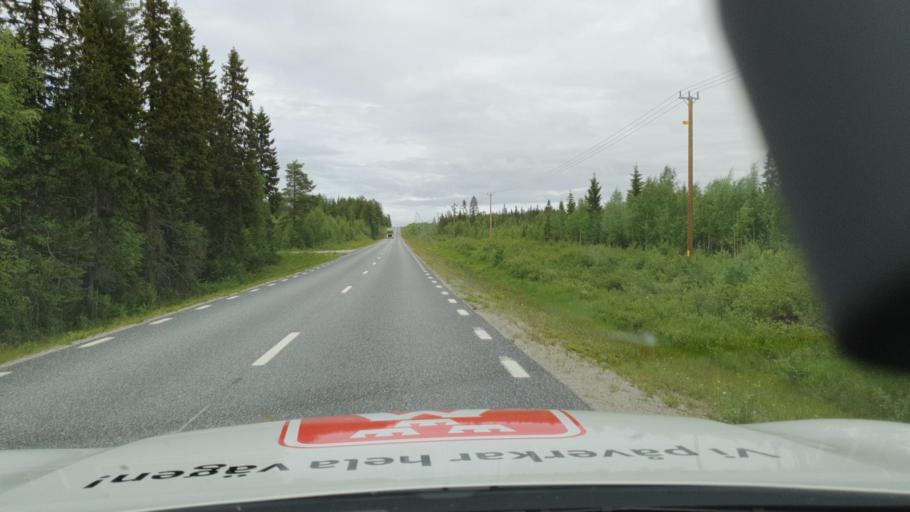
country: SE
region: Vaesterbotten
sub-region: Asele Kommun
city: Insjon
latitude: 64.3016
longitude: 17.6858
